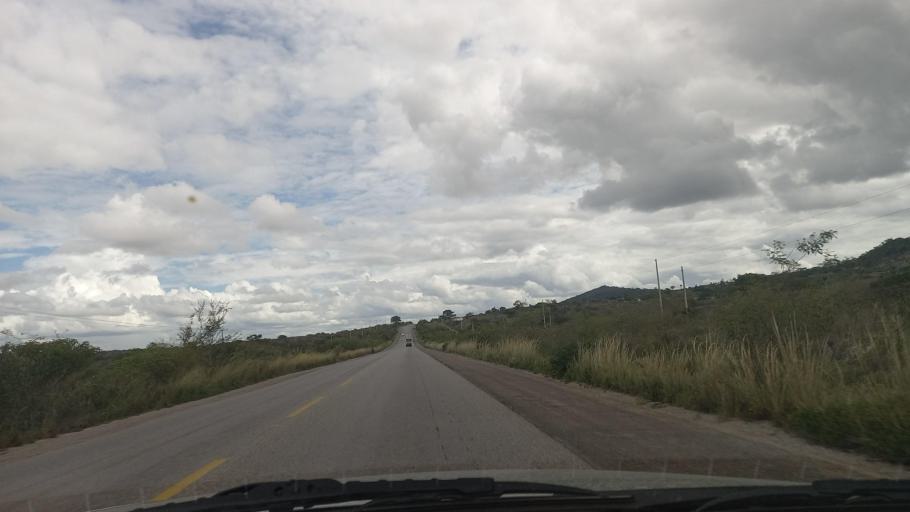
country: BR
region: Pernambuco
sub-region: Cachoeirinha
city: Cachoeirinha
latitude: -8.3399
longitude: -36.1596
